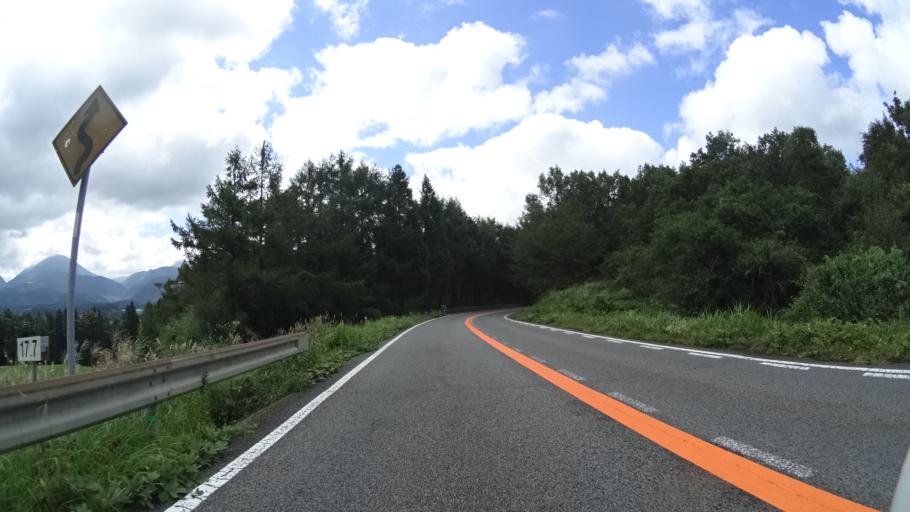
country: JP
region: Oita
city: Tsukawaki
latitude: 33.1687
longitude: 131.2483
